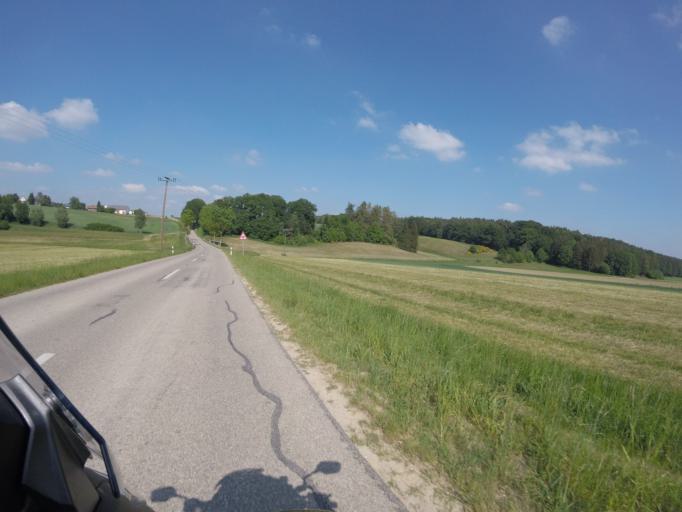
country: DE
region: Bavaria
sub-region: Upper Bavaria
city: Jetzendorf
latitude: 48.4599
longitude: 11.4284
